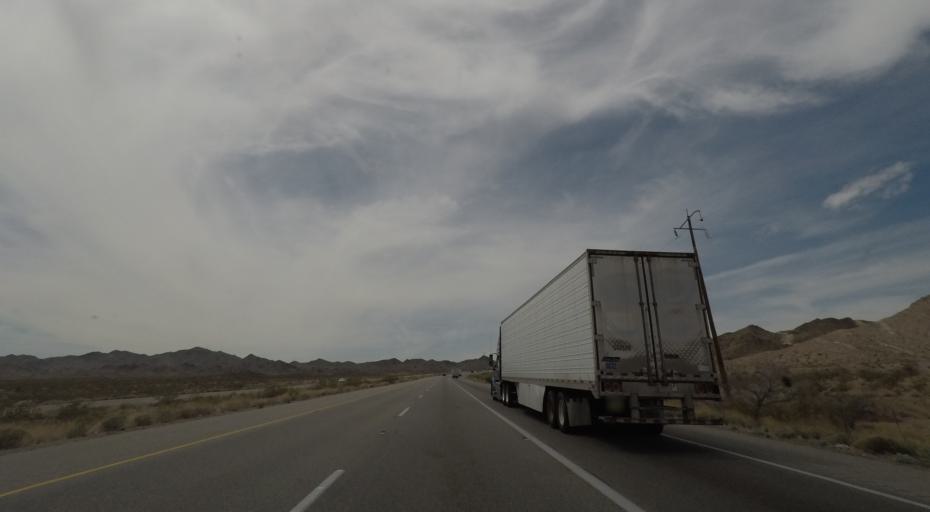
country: US
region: California
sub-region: San Bernardino County
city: Needles
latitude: 34.8307
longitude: -115.0226
